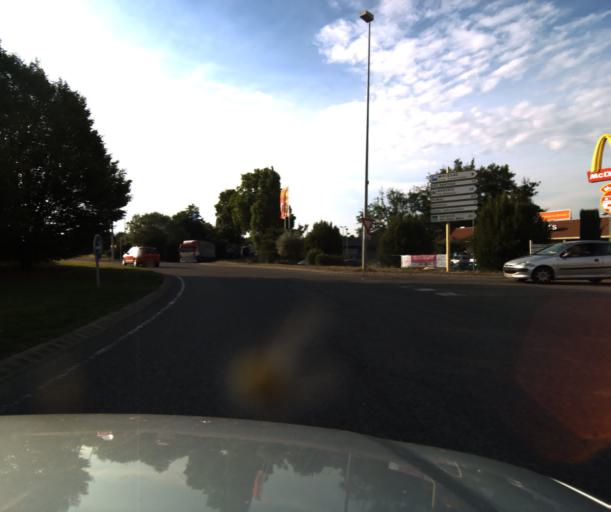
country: FR
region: Midi-Pyrenees
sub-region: Departement du Tarn-et-Garonne
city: Castelsarrasin
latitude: 44.0568
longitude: 1.0998
